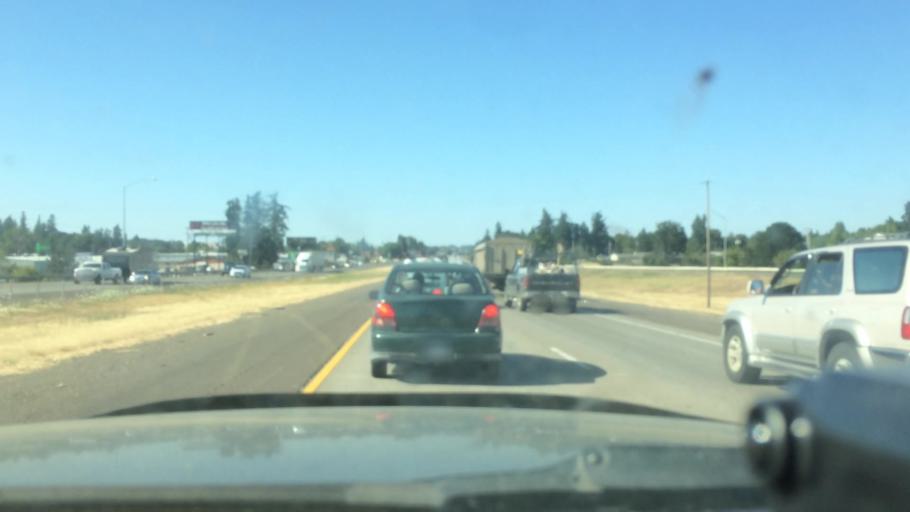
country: US
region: Oregon
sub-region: Linn County
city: Millersburg
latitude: 44.6462
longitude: -123.0624
